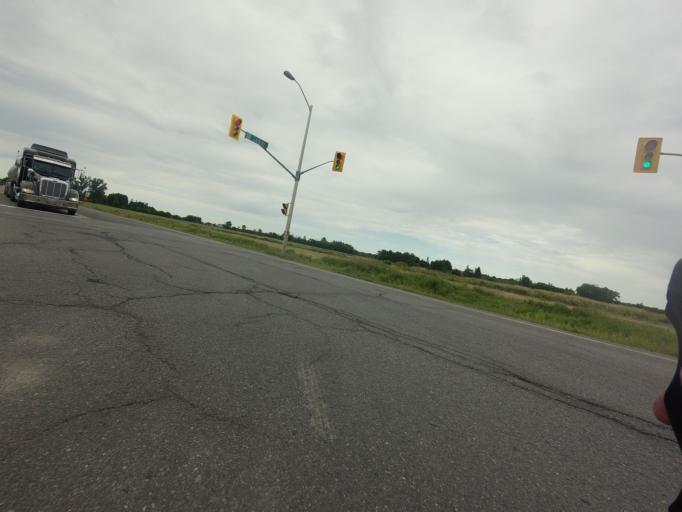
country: CA
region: Ontario
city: Ottawa
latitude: 45.3016
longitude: -75.7053
